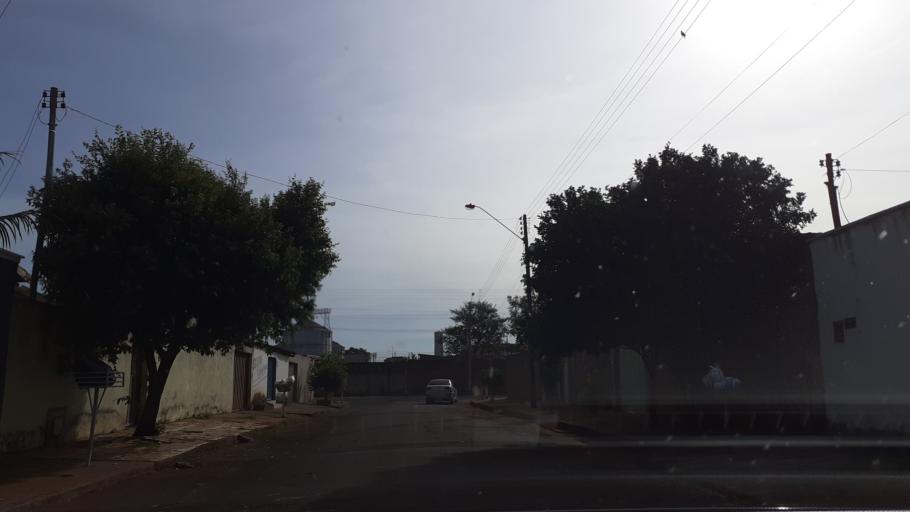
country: BR
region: Goias
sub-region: Itumbiara
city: Itumbiara
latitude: -18.4147
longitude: -49.2461
